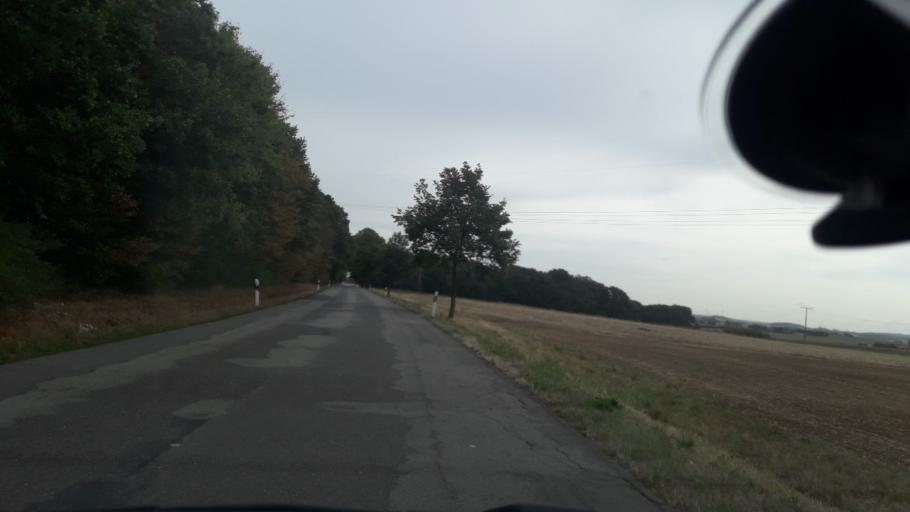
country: DE
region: Lower Saxony
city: Gross Twulpstedt
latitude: 52.3610
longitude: 10.9012
